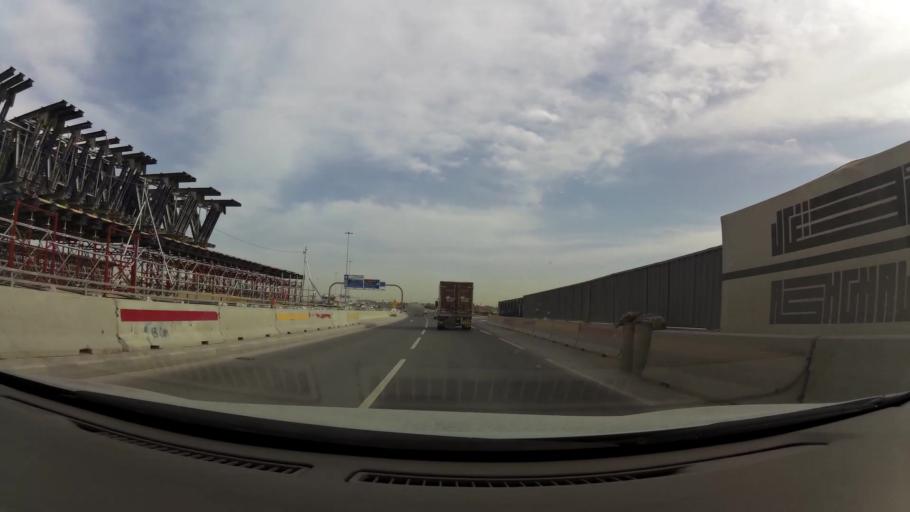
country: QA
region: Baladiyat ad Dawhah
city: Doha
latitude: 25.2936
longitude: 51.4753
